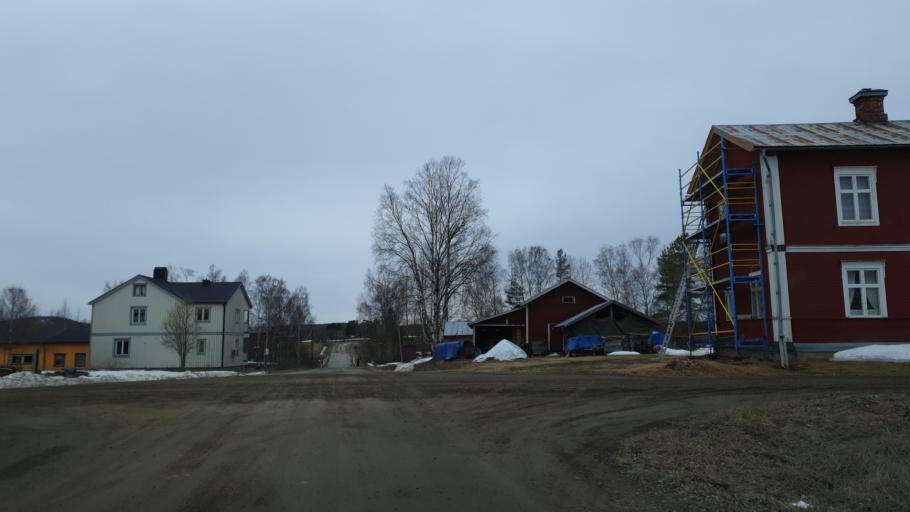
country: SE
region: Vaesterbotten
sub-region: Robertsfors Kommun
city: Robertsfors
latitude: 64.3822
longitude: 20.9193
